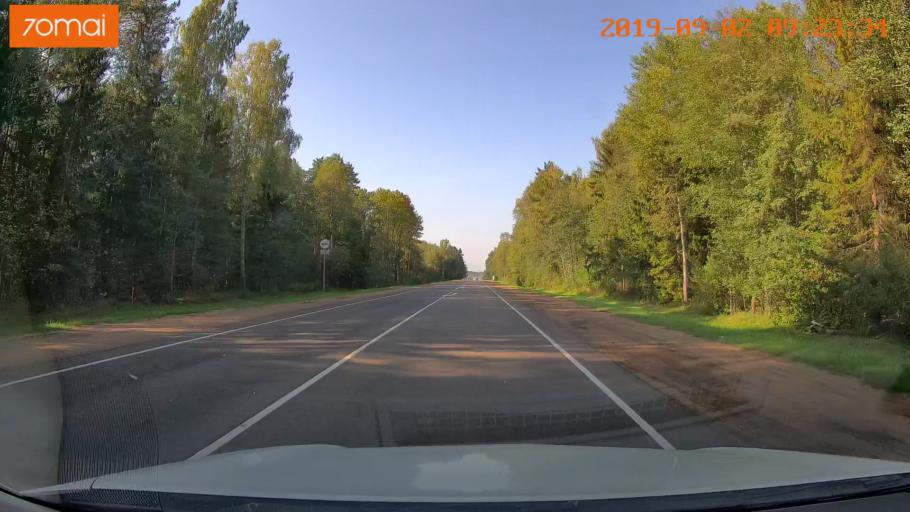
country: RU
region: Kaluga
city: Yukhnov
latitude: 54.7746
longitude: 35.3119
